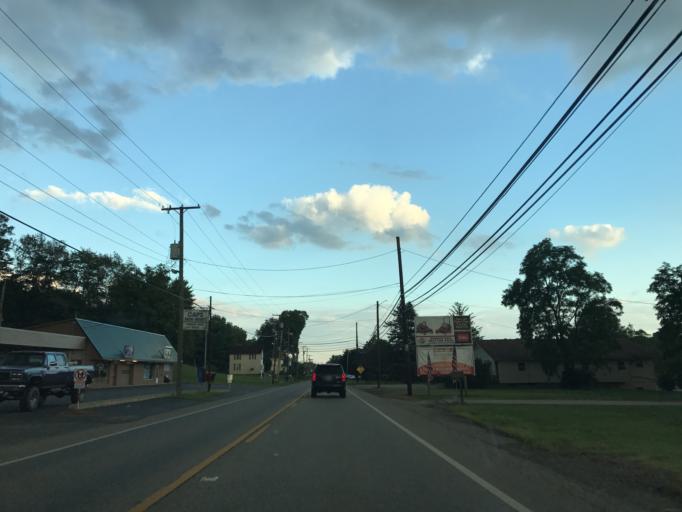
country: US
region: Ohio
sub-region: Stark County
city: Minerva
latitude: 40.7333
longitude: -81.1114
